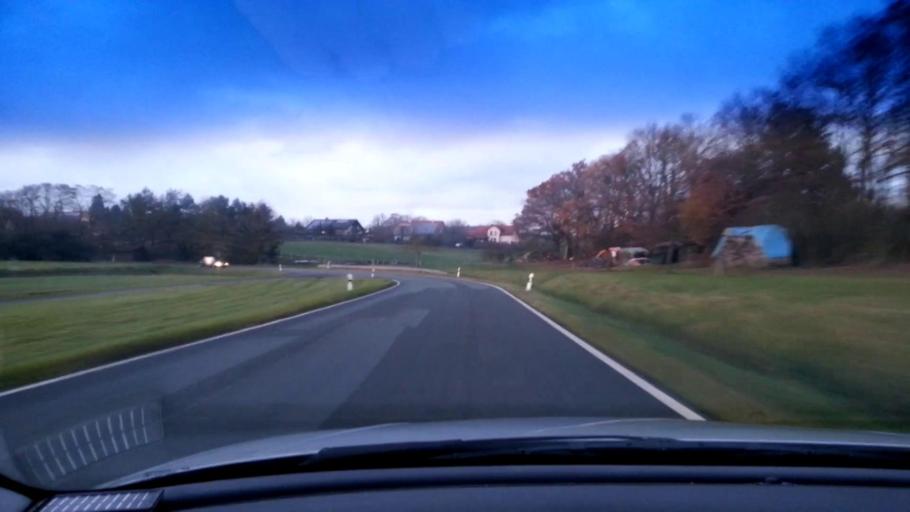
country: DE
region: Bavaria
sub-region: Upper Franconia
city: Frensdorf
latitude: 49.8321
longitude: 10.8762
